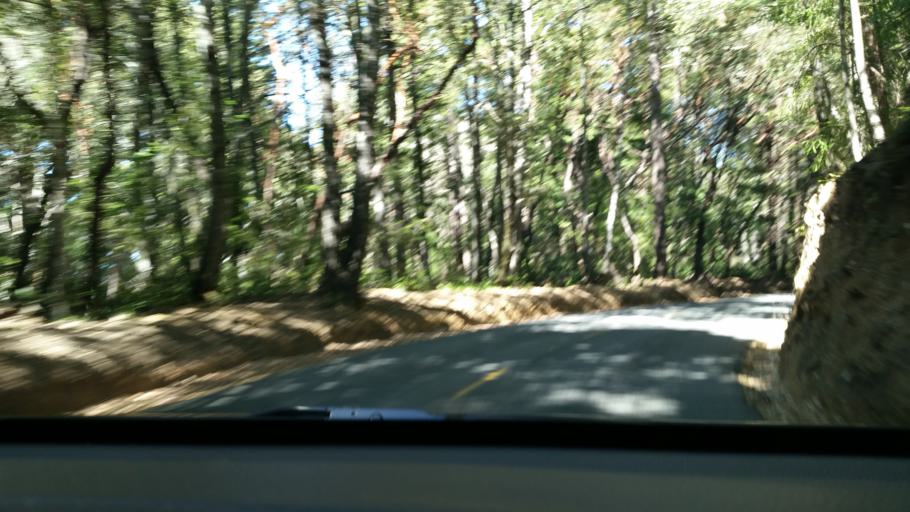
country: US
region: California
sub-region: San Mateo County
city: Emerald Lake Hills
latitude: 37.4334
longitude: -122.2987
